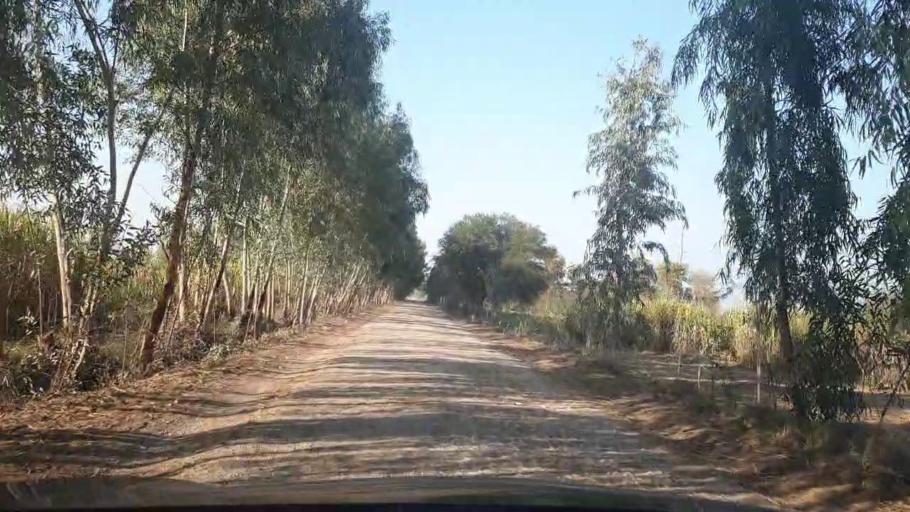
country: PK
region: Sindh
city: Ubauro
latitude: 28.1461
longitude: 69.6102
